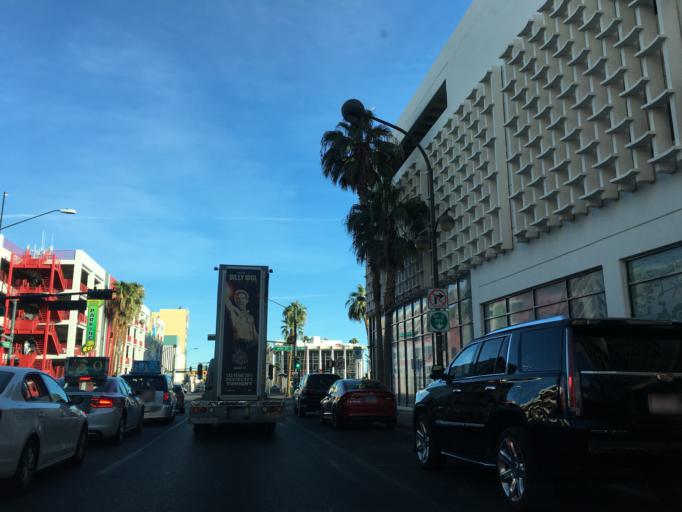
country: US
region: Nevada
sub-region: Clark County
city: Las Vegas
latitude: 36.1688
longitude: -115.1431
